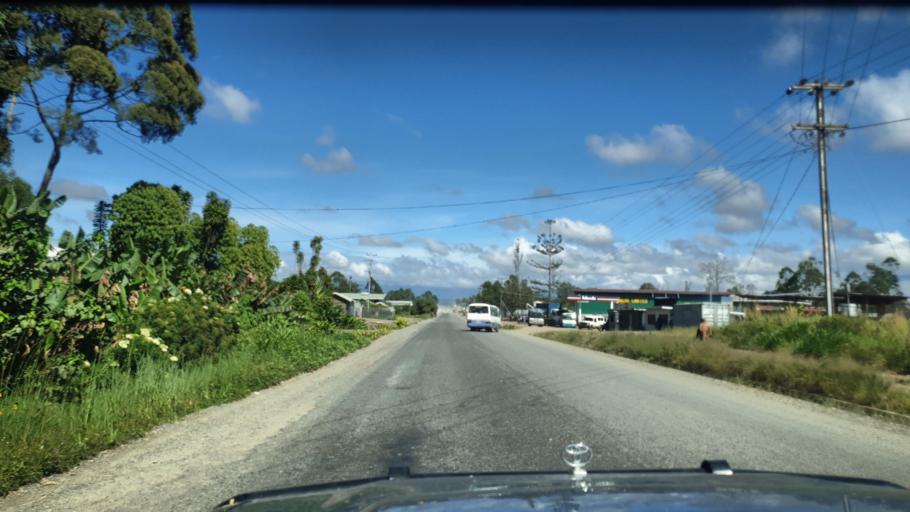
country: PG
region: Western Highlands
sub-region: Hagen
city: Mount Hagen
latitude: -5.8402
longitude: 144.3057
